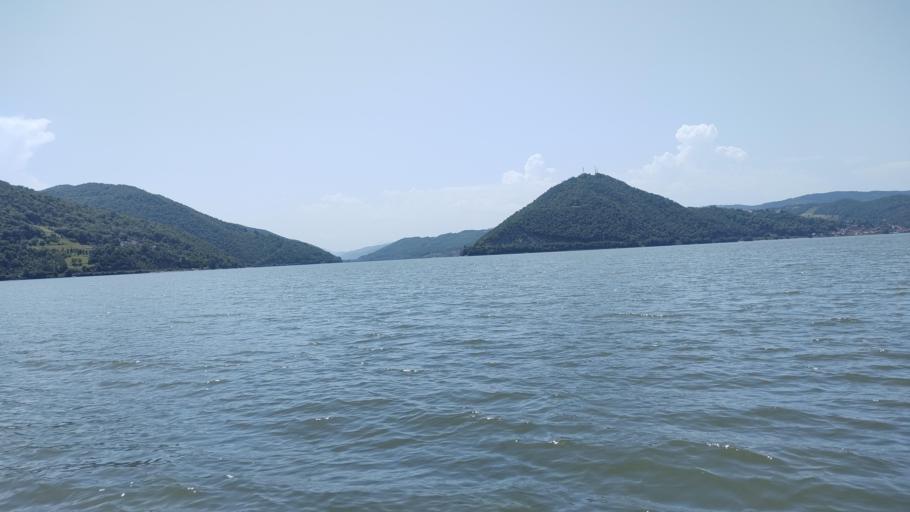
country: RO
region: Mehedinti
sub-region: Comuna Svinita
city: Svinita
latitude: 44.4825
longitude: 22.1775
